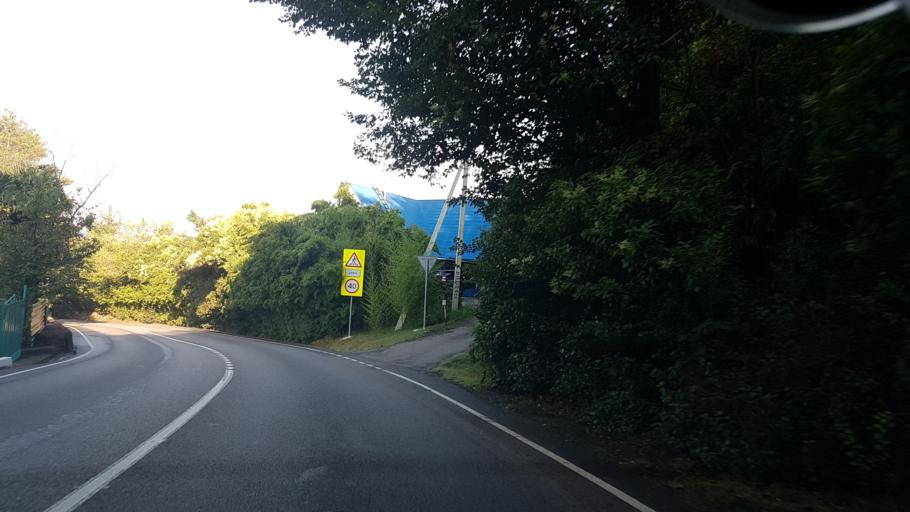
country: RU
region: Krasnodarskiy
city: Vardane
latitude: 43.7923
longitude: 39.4820
